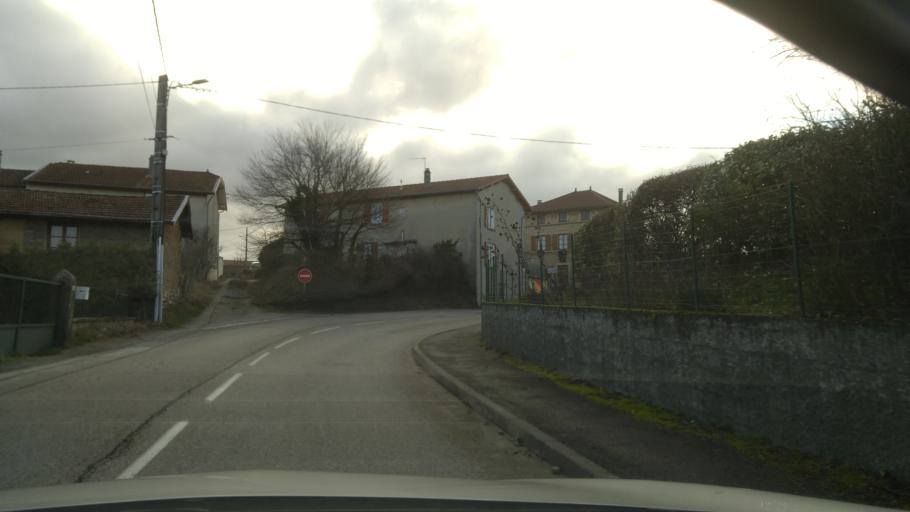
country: FR
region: Rhone-Alpes
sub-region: Departement de l'Isere
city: Roche
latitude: 45.5871
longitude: 5.1626
